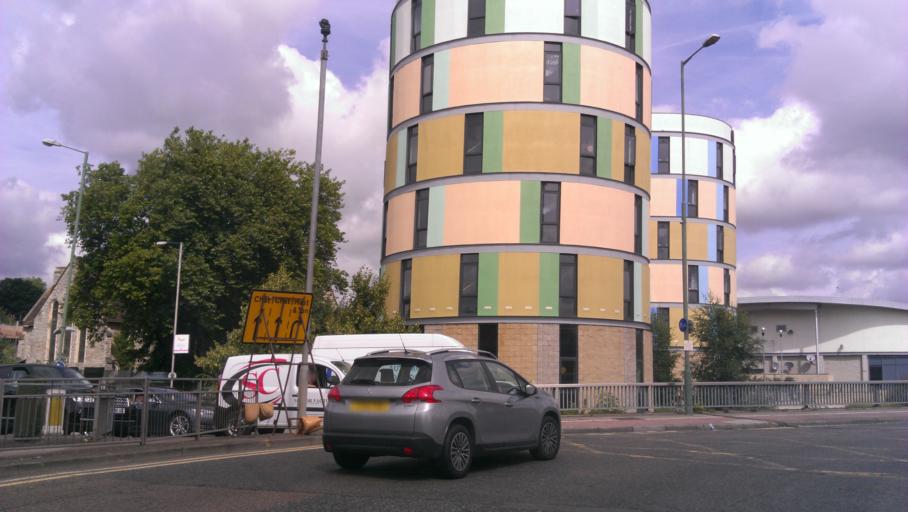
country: GB
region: England
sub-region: Kent
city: Maidstone
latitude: 51.2721
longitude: 0.5172
